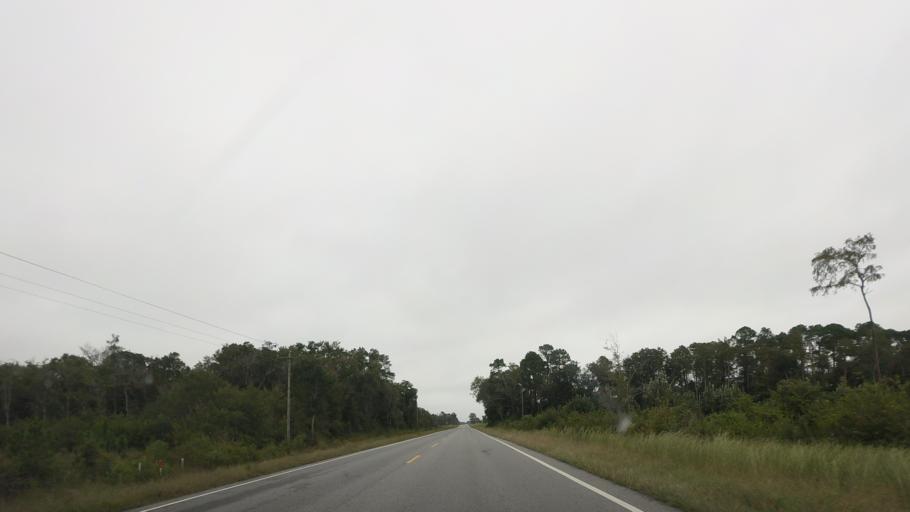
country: US
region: Georgia
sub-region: Berrien County
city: Enigma
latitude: 31.3410
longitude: -83.2290
